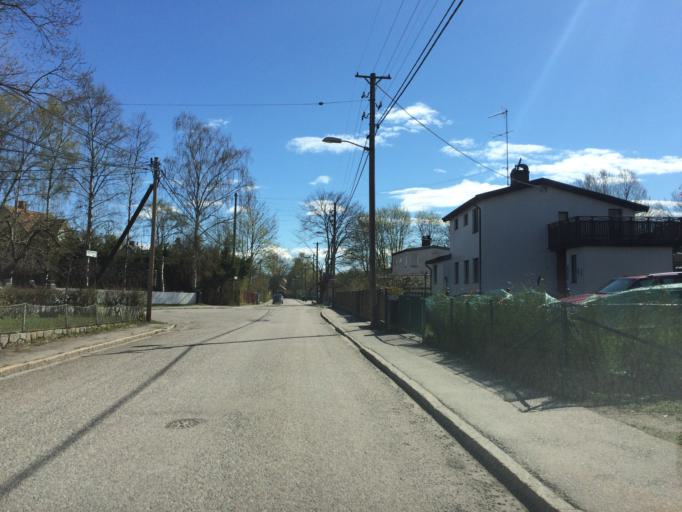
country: SE
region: Stockholm
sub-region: Huddinge Kommun
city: Huddinge
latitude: 59.2773
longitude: 17.9838
